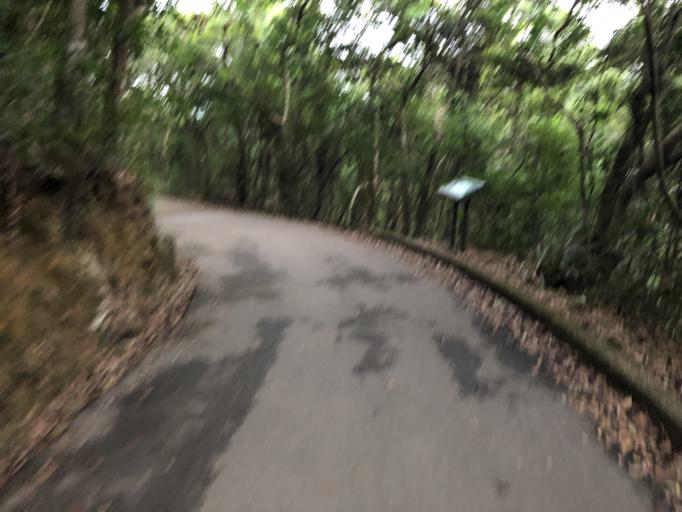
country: HK
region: Wanchai
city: Wan Chai
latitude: 22.2652
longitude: 114.2147
